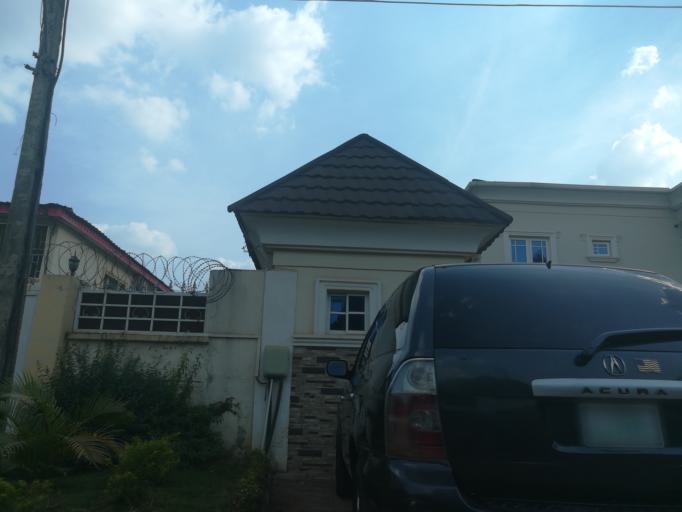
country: NG
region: Abuja Federal Capital Territory
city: Abuja
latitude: 9.0842
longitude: 7.4153
